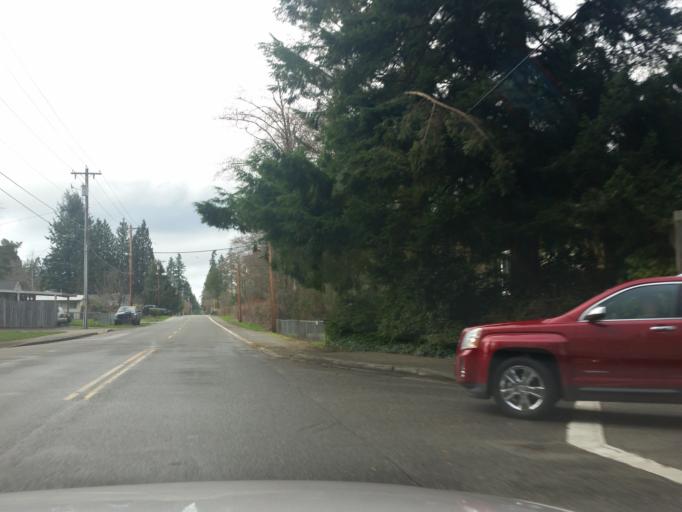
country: US
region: Washington
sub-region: Snohomish County
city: Meadowdale
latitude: 47.8550
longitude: -122.3091
